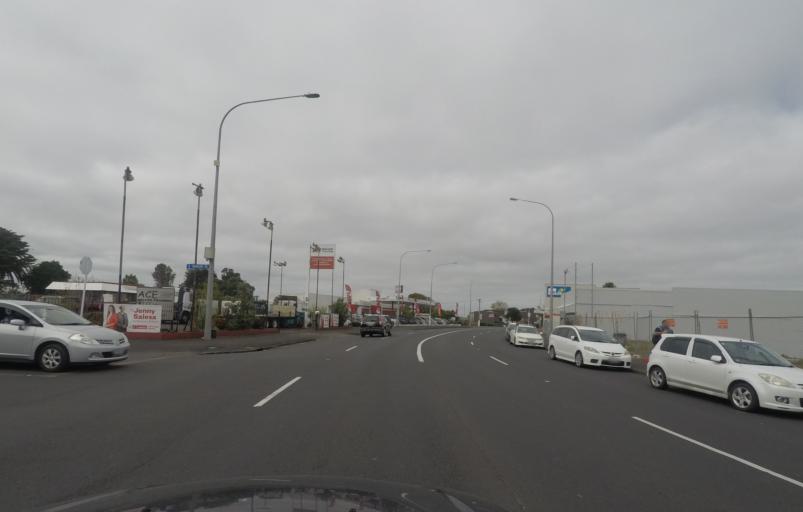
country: NZ
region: Auckland
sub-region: Auckland
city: Mangere
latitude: -36.9476
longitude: 174.8458
